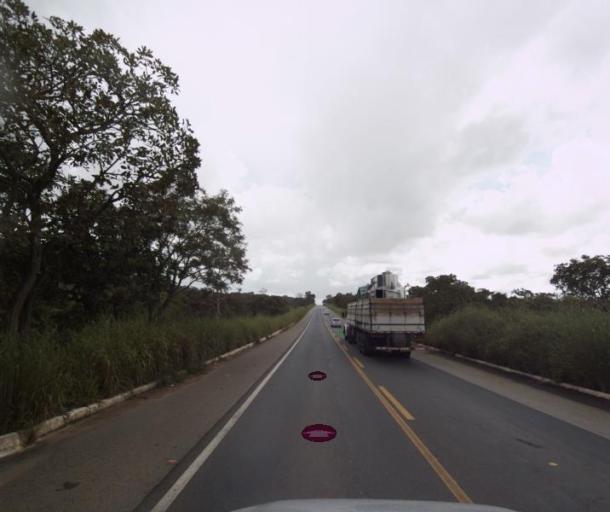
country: BR
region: Goias
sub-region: Uruacu
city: Uruacu
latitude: -14.2278
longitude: -49.1333
